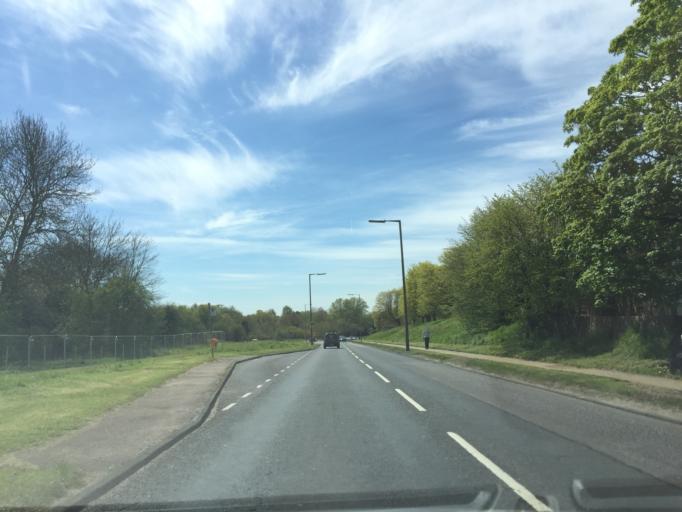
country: GB
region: England
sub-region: Essex
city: Harlow
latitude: 51.7634
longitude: 0.0890
